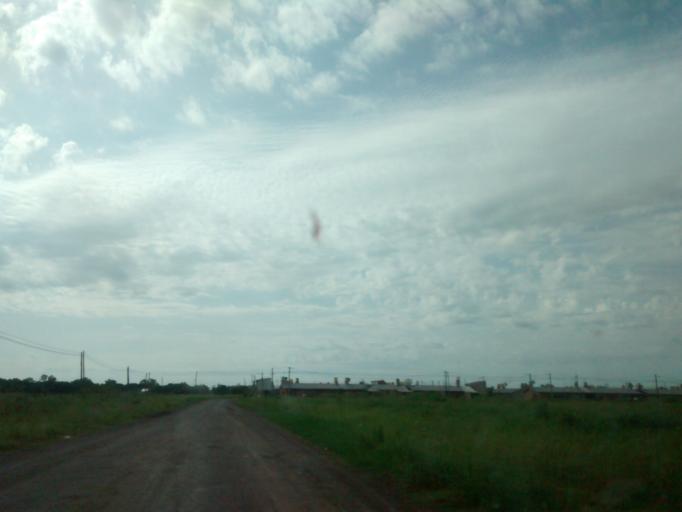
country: AR
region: Chaco
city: Resistencia
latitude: -27.4086
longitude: -58.9627
